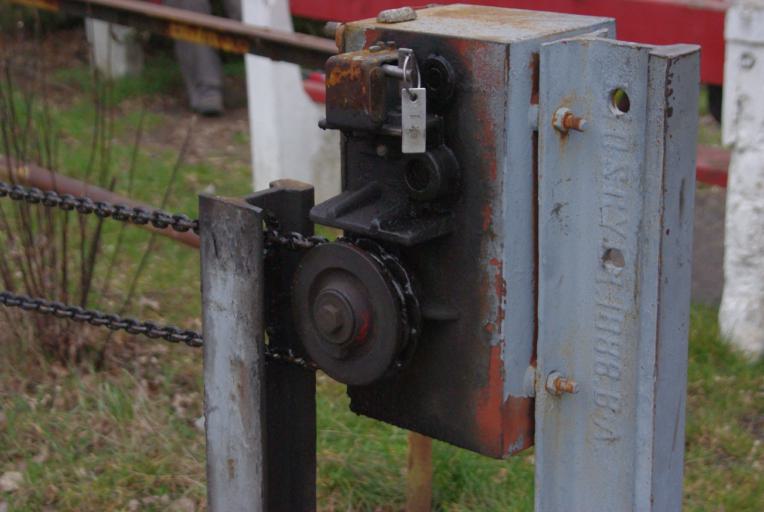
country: HU
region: Nograd
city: Diosjeno
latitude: 47.9023
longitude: 19.0471
